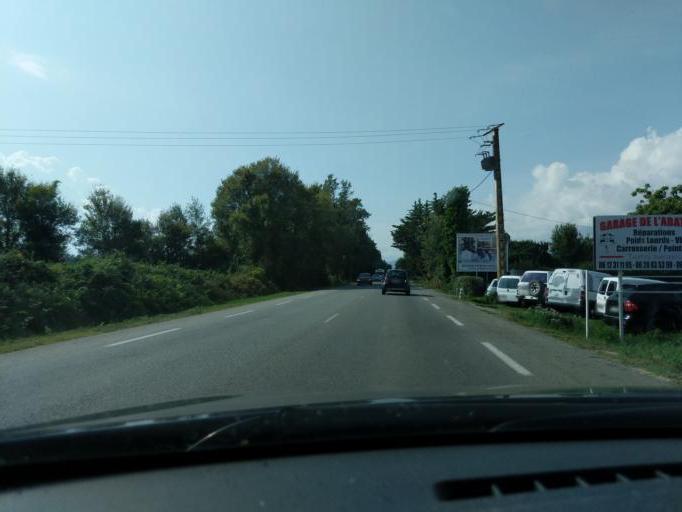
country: FR
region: Corsica
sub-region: Departement de la Haute-Corse
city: Ghisonaccia
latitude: 41.9736
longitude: 9.3990
